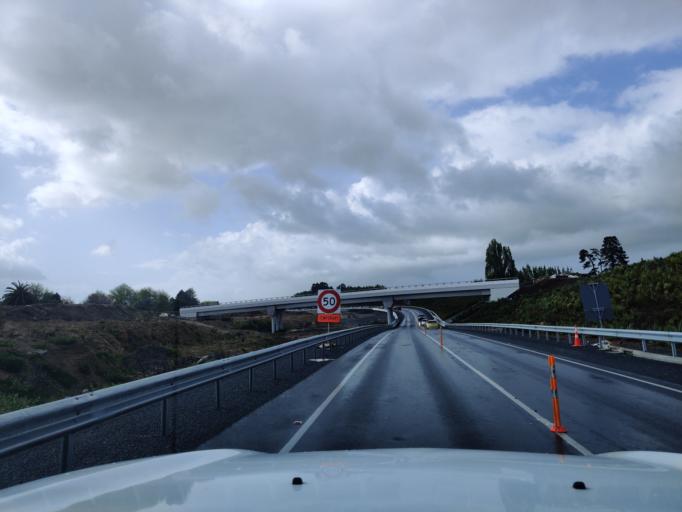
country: NZ
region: Waikato
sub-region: Hamilton City
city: Hamilton
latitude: -37.8153
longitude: 175.3418
